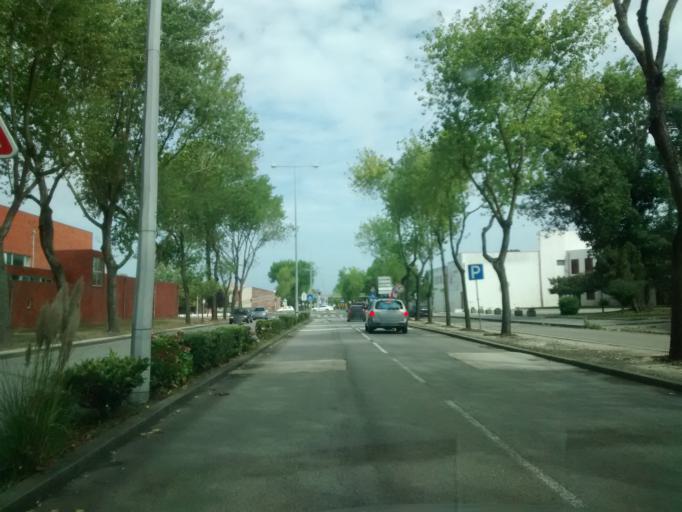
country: PT
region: Aveiro
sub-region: Aveiro
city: Aradas
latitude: 40.6296
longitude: -8.6535
